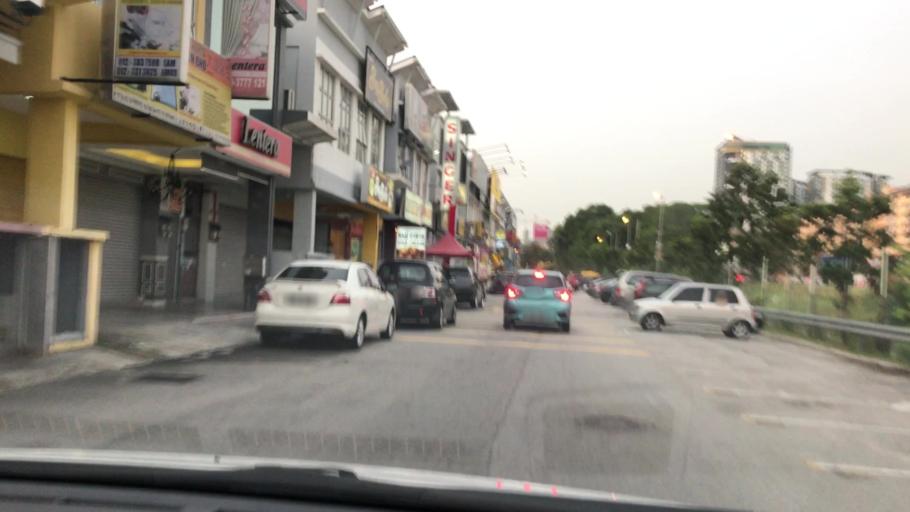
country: MY
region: Putrajaya
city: Putrajaya
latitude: 2.9890
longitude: 101.6713
